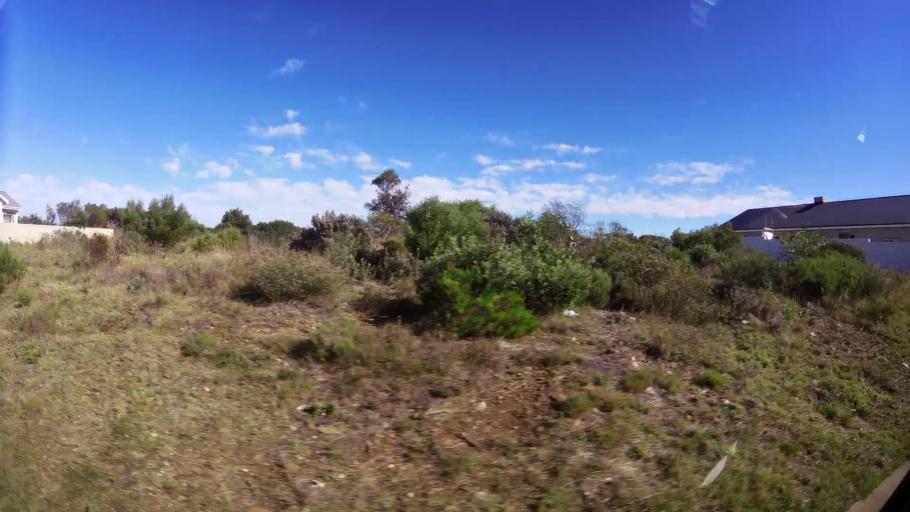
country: ZA
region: Eastern Cape
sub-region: Cacadu District Municipality
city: Jeffrey's Bay
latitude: -34.0334
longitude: 24.9085
